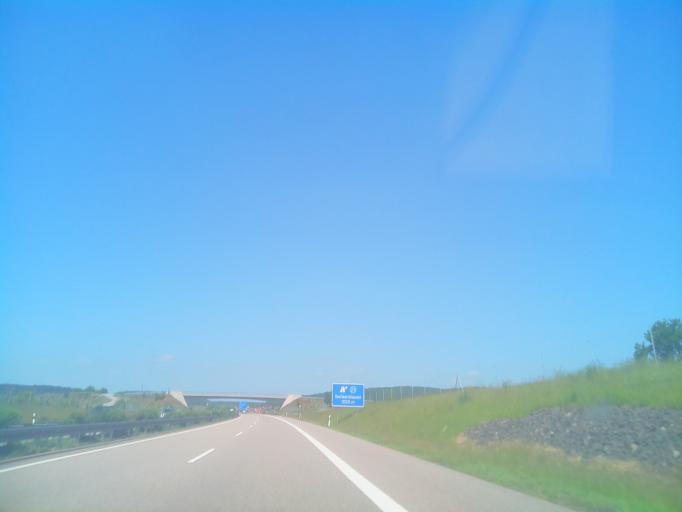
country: DE
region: Thuringia
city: Wolfershausen
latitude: 50.4372
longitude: 10.4343
